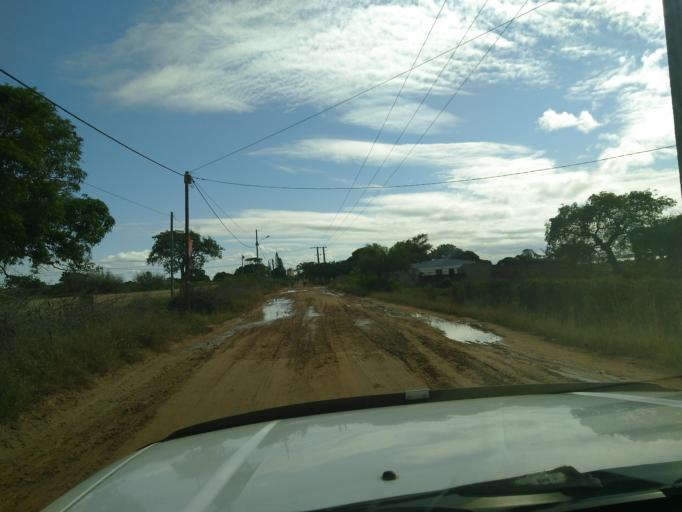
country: MZ
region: Maputo City
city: Maputo
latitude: -25.9950
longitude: 32.5373
